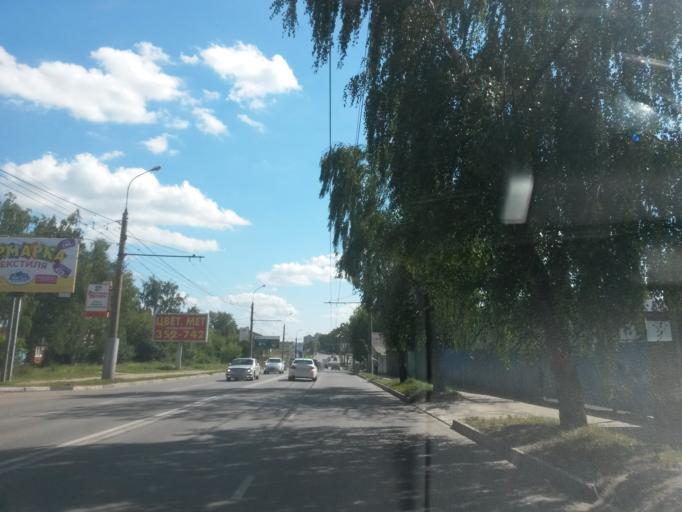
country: RU
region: Ivanovo
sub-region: Gorod Ivanovo
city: Ivanovo
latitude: 56.9776
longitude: 41.0047
